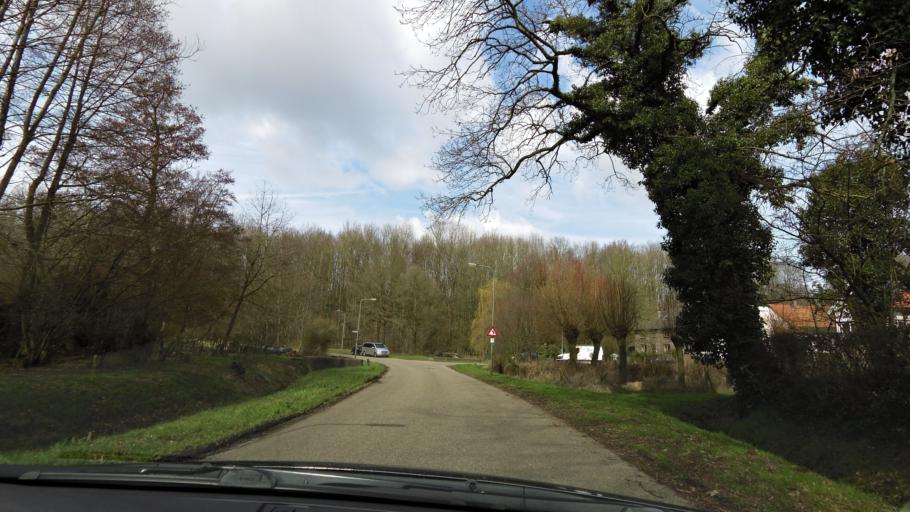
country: NL
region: Limburg
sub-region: Gemeente Simpelveld
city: Simpelveld
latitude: 50.8275
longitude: 5.9985
